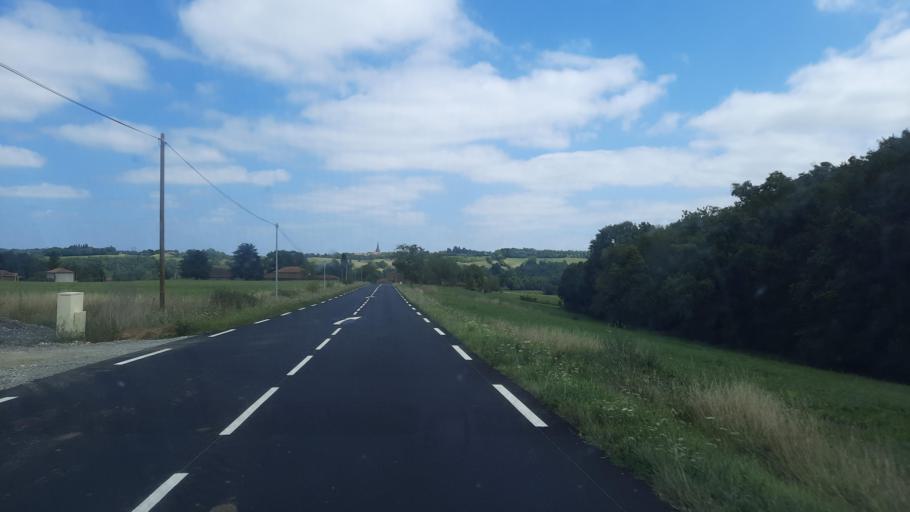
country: FR
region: Midi-Pyrenees
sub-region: Departement de la Haute-Garonne
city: Boulogne-sur-Gesse
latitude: 43.2967
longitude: 0.6181
